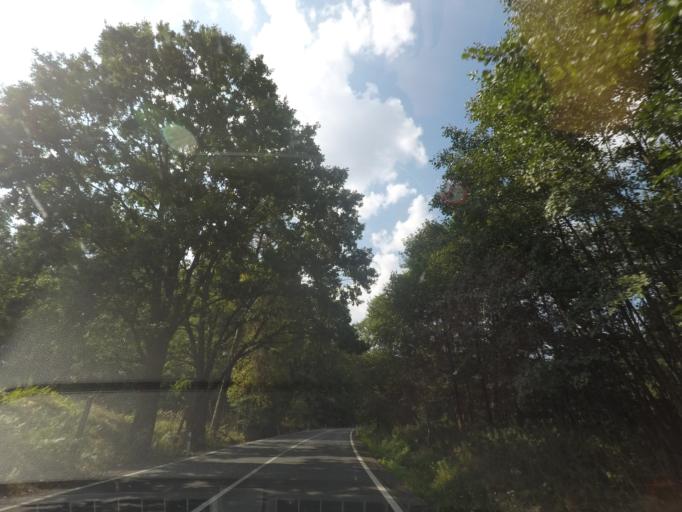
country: CZ
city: Borohradek
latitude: 50.1070
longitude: 16.0790
